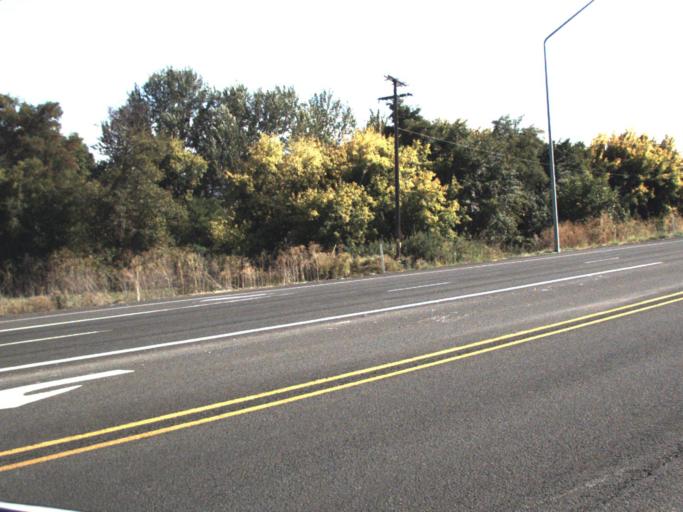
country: US
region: Washington
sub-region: Walla Walla County
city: College Place
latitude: 46.0233
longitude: -118.3890
